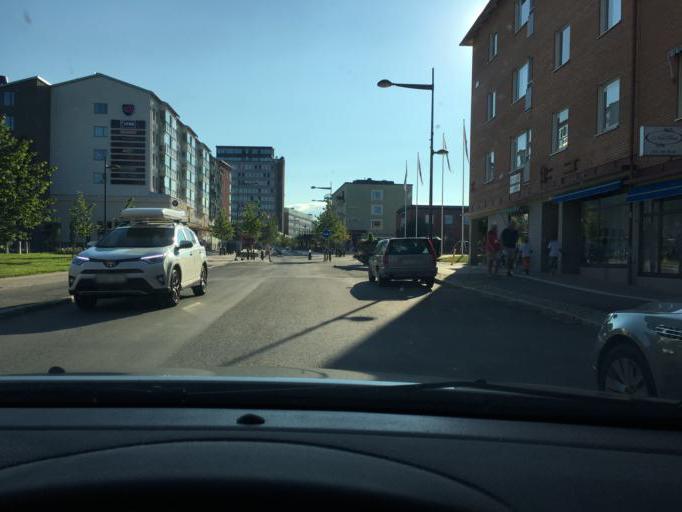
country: SE
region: Norrbotten
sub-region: Bodens Kommun
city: Boden
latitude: 65.8256
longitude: 21.6922
